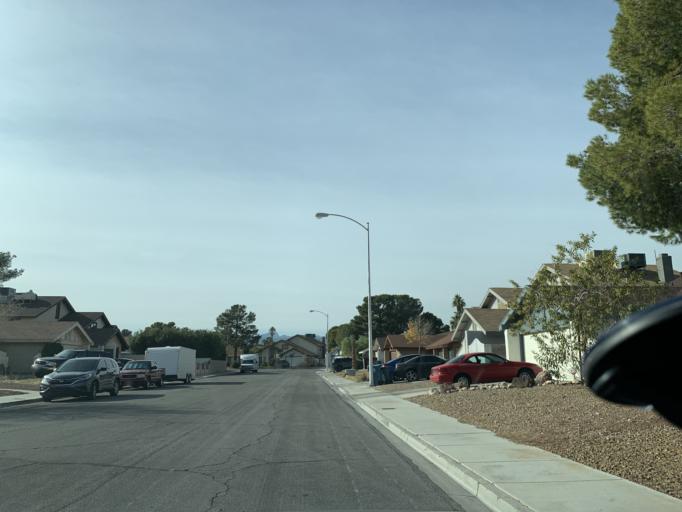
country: US
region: Nevada
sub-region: Clark County
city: Spring Valley
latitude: 36.1060
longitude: -115.2353
